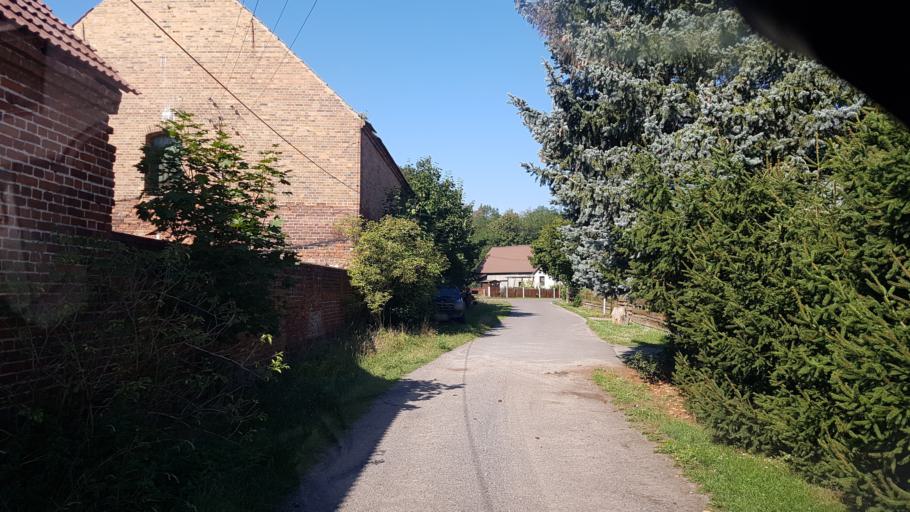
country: DE
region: Brandenburg
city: Vetschau
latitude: 51.7491
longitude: 14.0398
